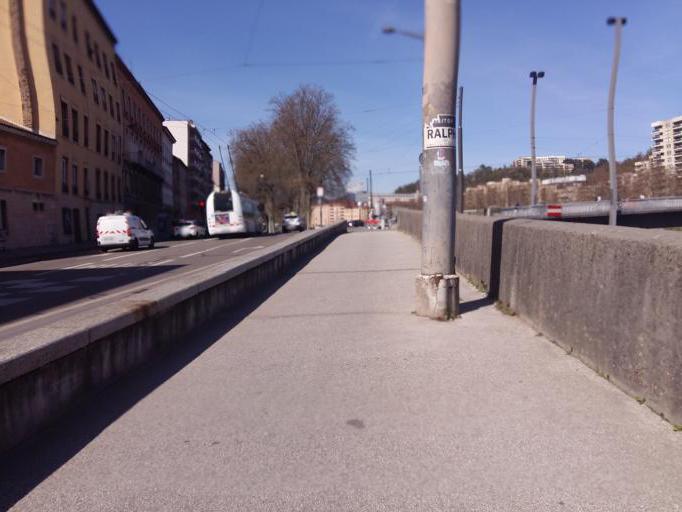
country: FR
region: Rhone-Alpes
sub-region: Departement du Rhone
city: Tassin-la-Demi-Lune
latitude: 45.7694
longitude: 4.8128
